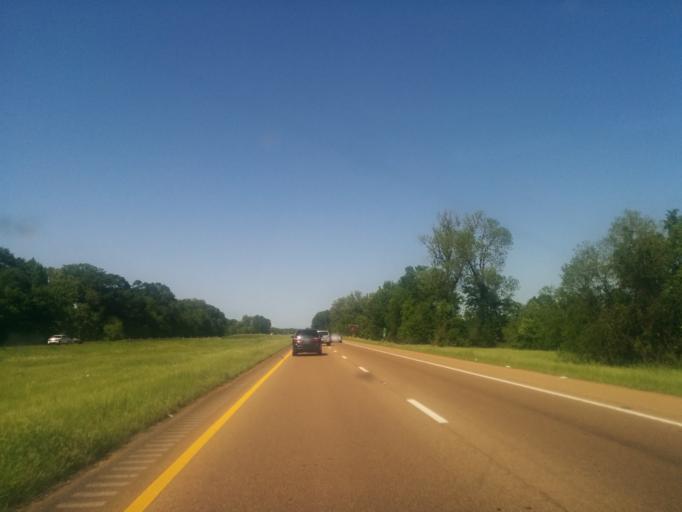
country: US
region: Mississippi
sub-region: Madison County
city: Madison
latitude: 32.4901
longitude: -90.1274
